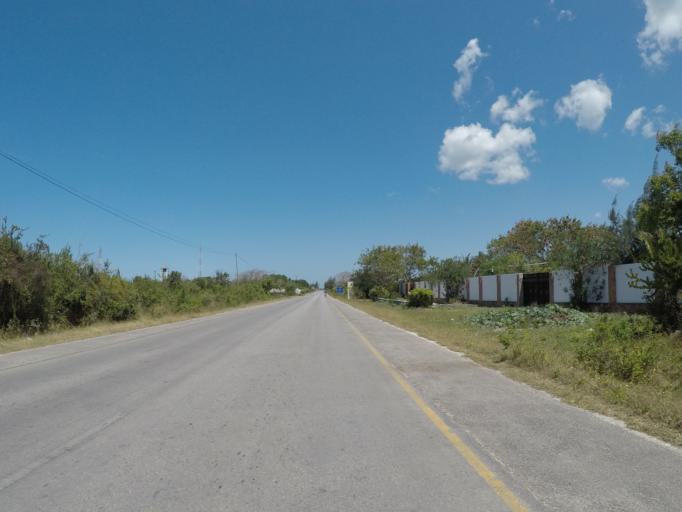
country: TZ
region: Zanzibar Central/South
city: Nganane
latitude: -6.2947
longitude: 39.5376
